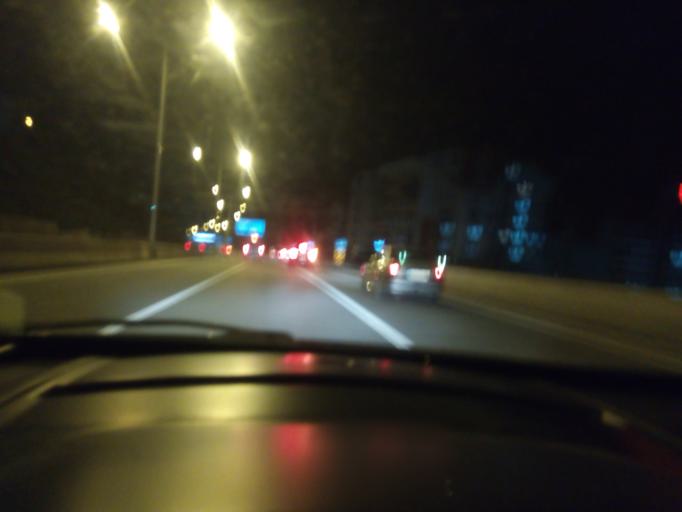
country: TR
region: Bursa
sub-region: Mudanya
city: Mudanya
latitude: 40.3476
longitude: 28.9229
